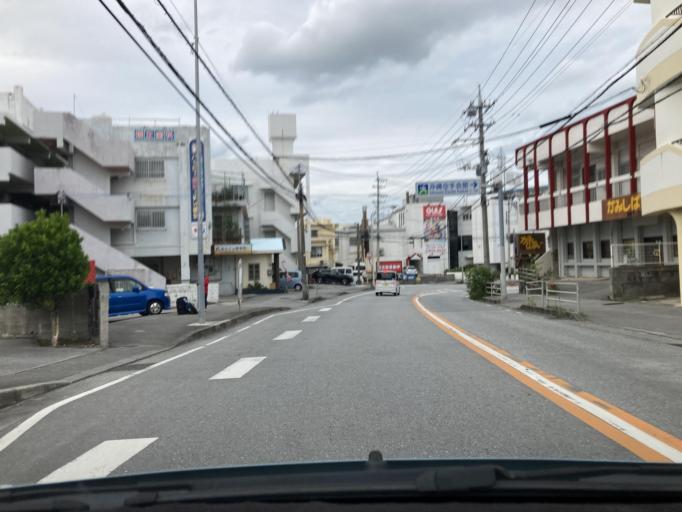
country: JP
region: Okinawa
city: Tomigusuku
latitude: 26.1868
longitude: 127.6804
